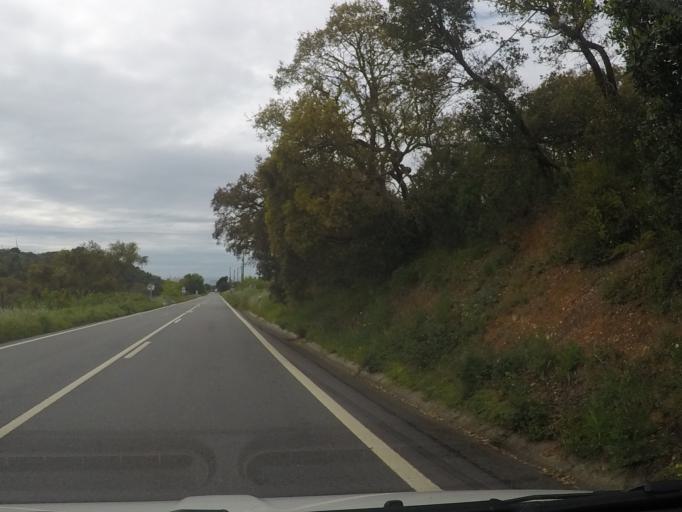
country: PT
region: Setubal
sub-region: Sines
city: Porto Covo
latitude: 37.8659
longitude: -8.7296
